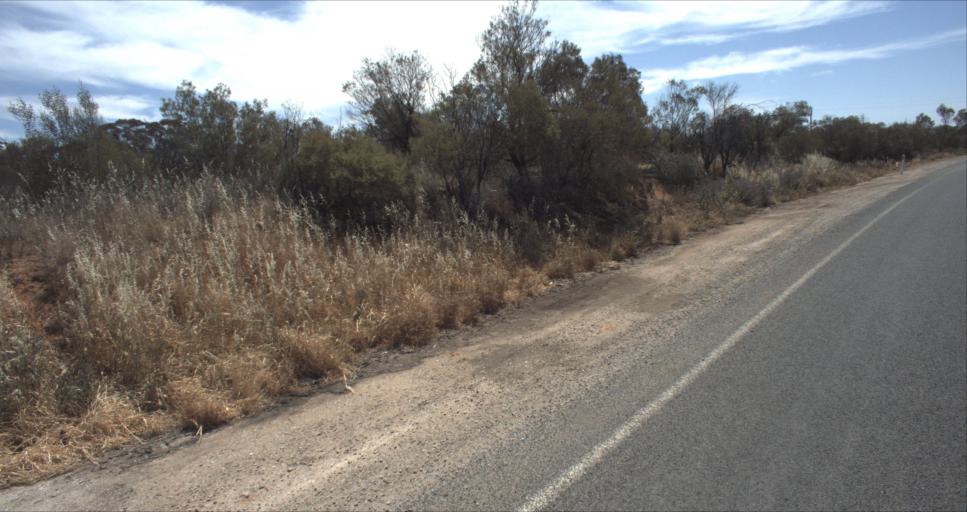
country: AU
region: New South Wales
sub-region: Leeton
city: Leeton
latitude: -34.6636
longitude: 146.4487
